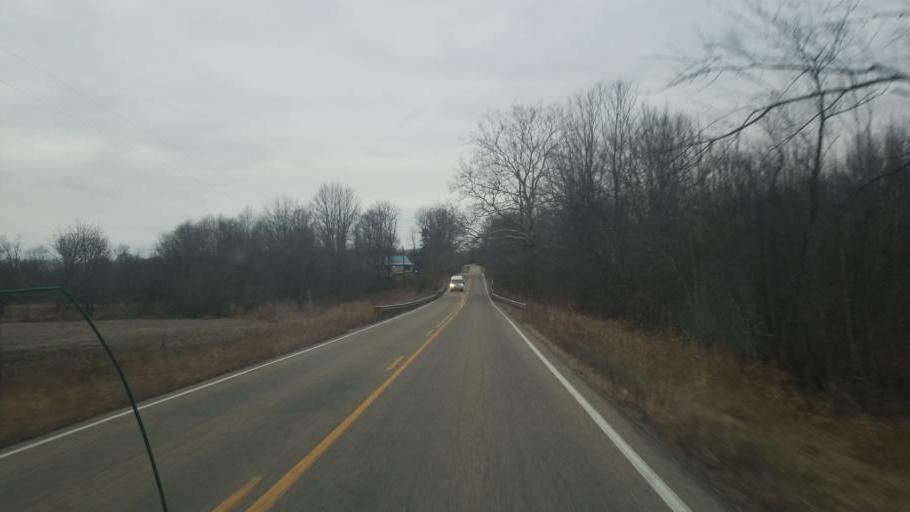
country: US
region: Indiana
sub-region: Owen County
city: Spencer
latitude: 39.3524
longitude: -86.9300
